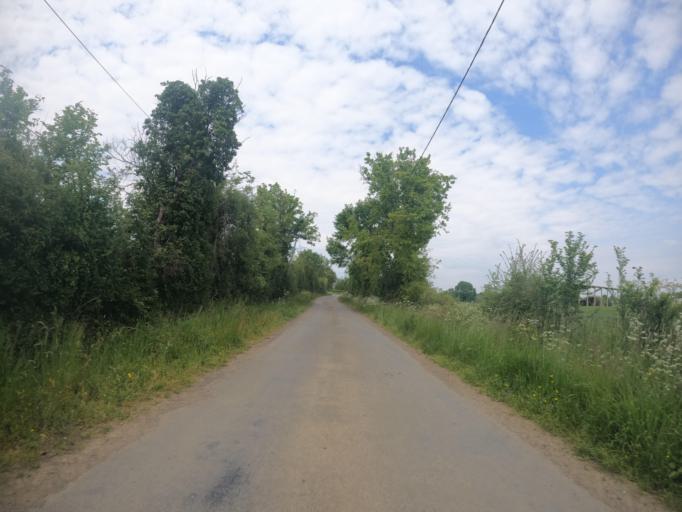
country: FR
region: Poitou-Charentes
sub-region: Departement des Deux-Sevres
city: Saint-Varent
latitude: 46.8721
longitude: -0.2780
